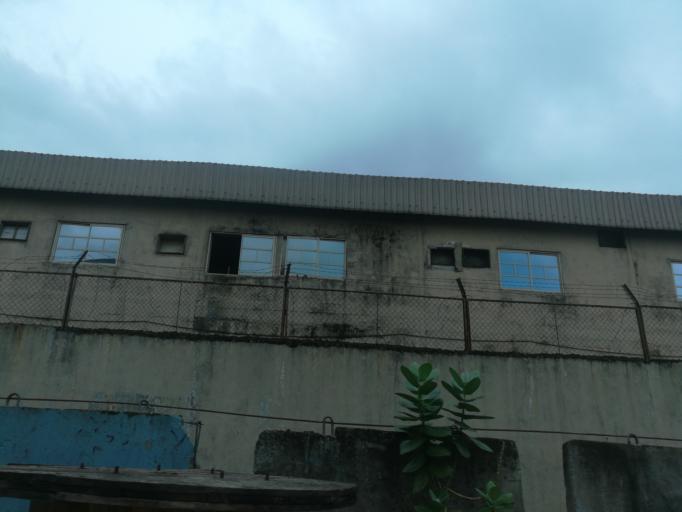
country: NG
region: Lagos
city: Ikeja
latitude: 6.6096
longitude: 3.3420
